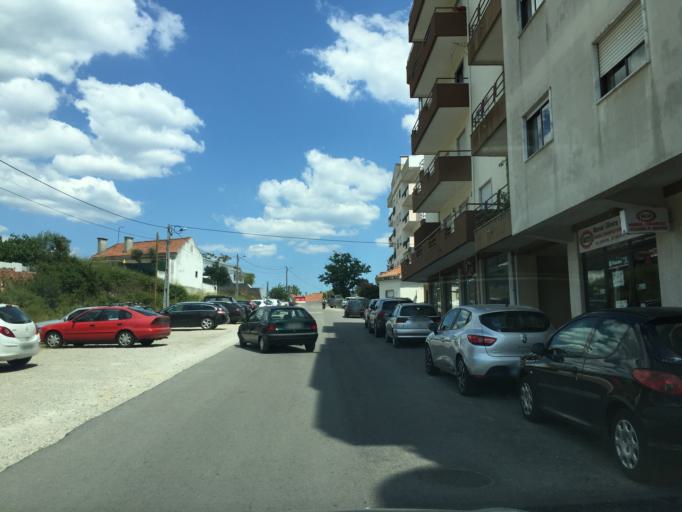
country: PT
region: Santarem
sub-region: Ourem
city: Ourem
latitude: 39.6580
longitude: -8.5754
